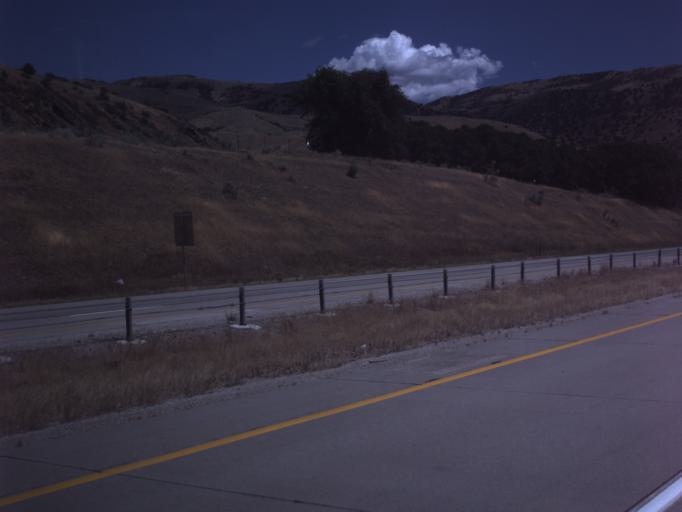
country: US
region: Utah
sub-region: Morgan County
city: Morgan
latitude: 41.0482
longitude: -111.6401
